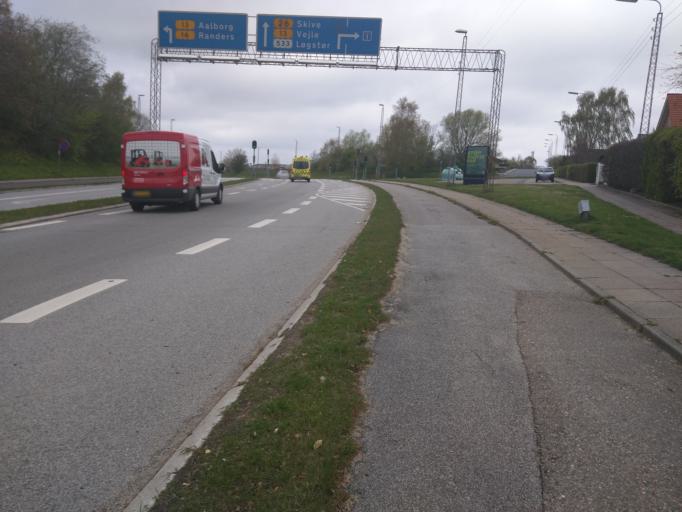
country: DK
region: Central Jutland
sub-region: Viborg Kommune
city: Viborg
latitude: 56.4667
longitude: 9.4161
